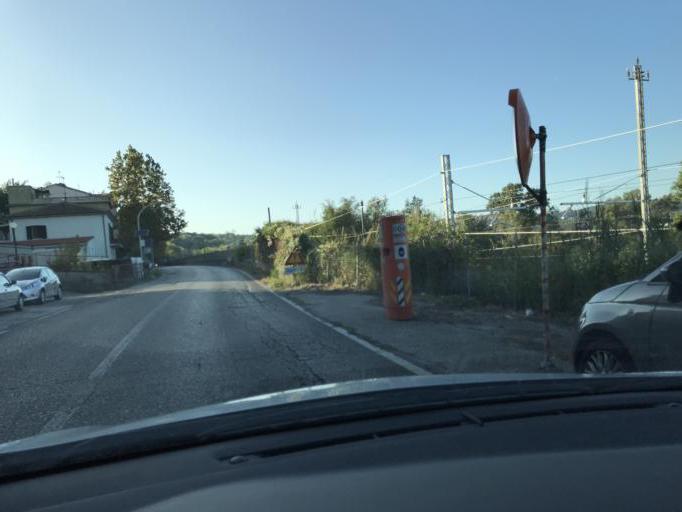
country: IT
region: Latium
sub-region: Provincia di Viterbo
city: Orte Scalo
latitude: 42.4455
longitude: 12.3977
